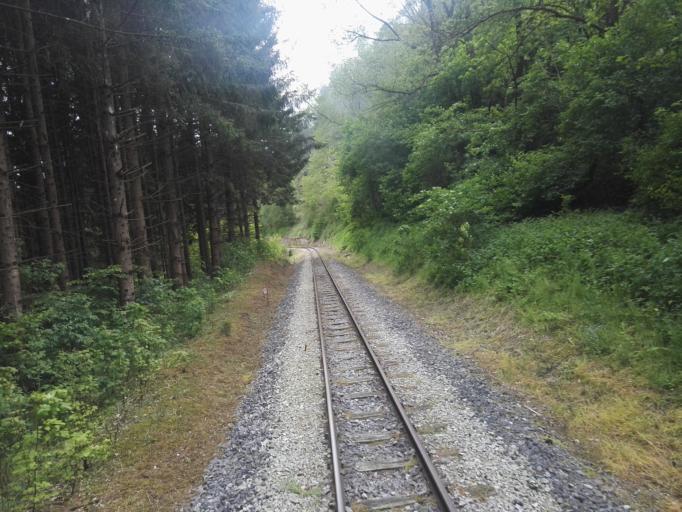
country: AT
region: Styria
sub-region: Politischer Bezirk Weiz
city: Birkfeld
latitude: 47.3500
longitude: 15.6968
